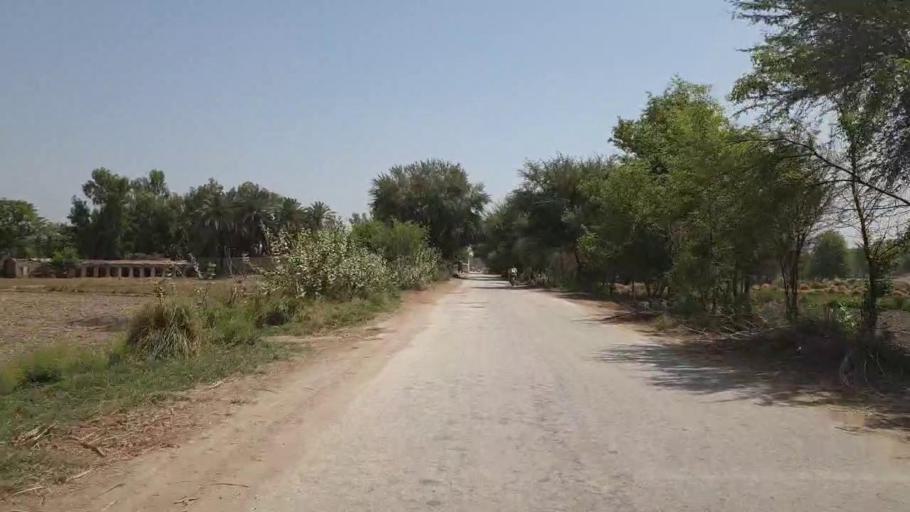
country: PK
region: Sindh
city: Adilpur
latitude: 27.8243
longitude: 69.2470
